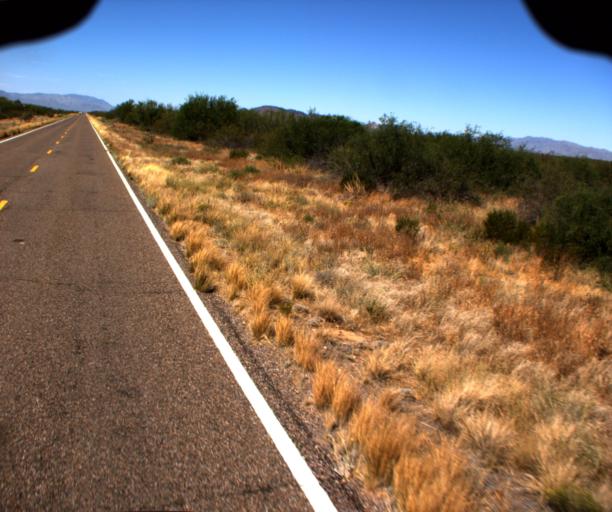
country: US
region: Arizona
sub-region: Yavapai County
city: Congress
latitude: 34.0783
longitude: -113.0234
